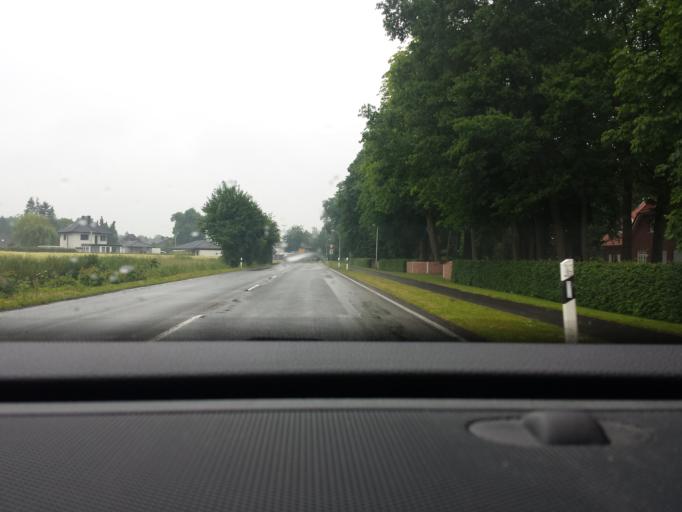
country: DE
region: North Rhine-Westphalia
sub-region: Regierungsbezirk Munster
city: Gronau
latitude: 52.2133
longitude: 6.9867
